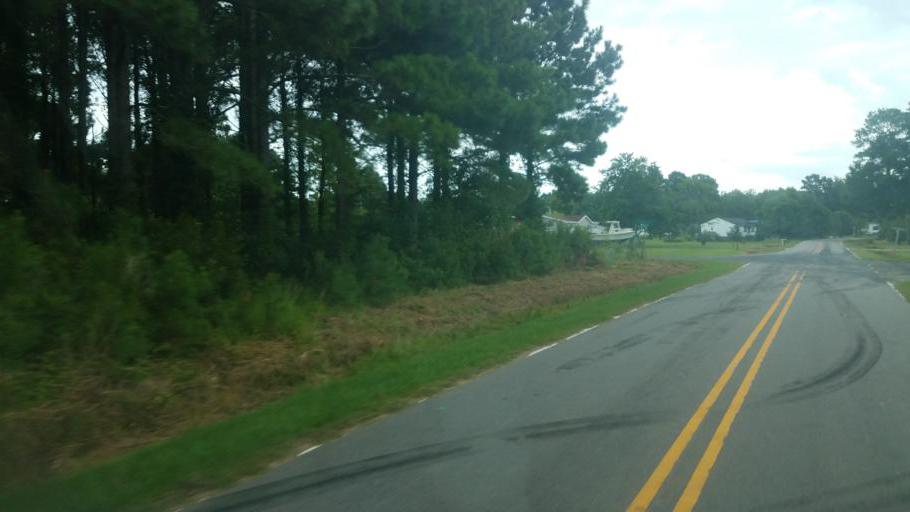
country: US
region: North Carolina
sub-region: Tyrrell County
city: Columbia
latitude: 35.9464
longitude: -76.3081
